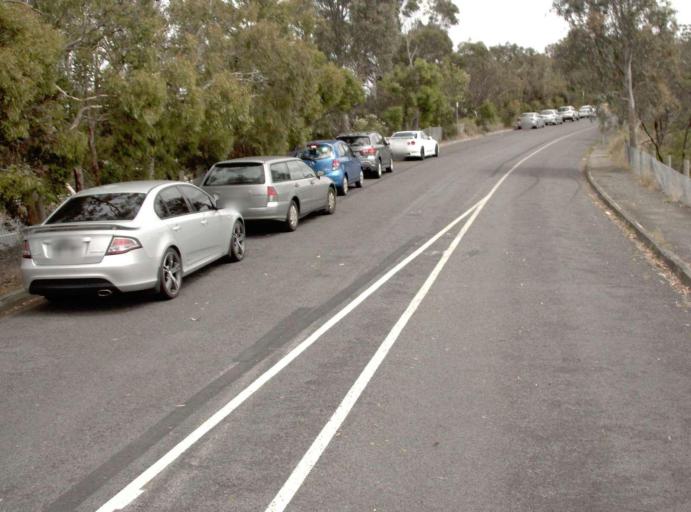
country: AU
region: Victoria
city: Abbotsford
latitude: -37.8013
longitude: 145.0067
